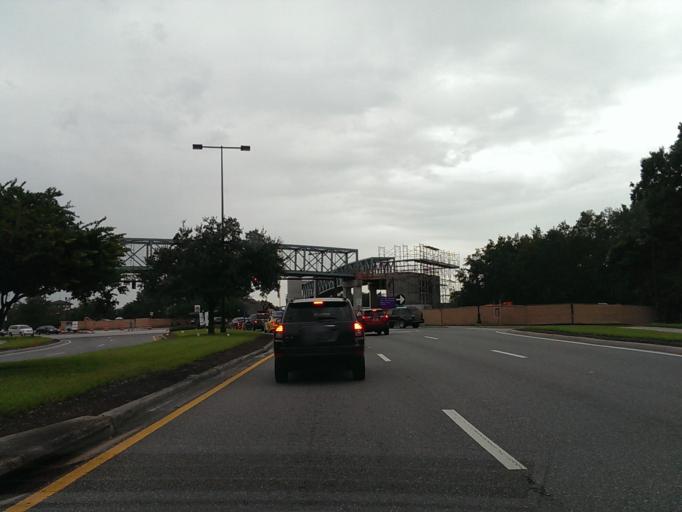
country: US
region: Florida
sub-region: Osceola County
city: Celebration
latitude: 28.3738
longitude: -81.5123
